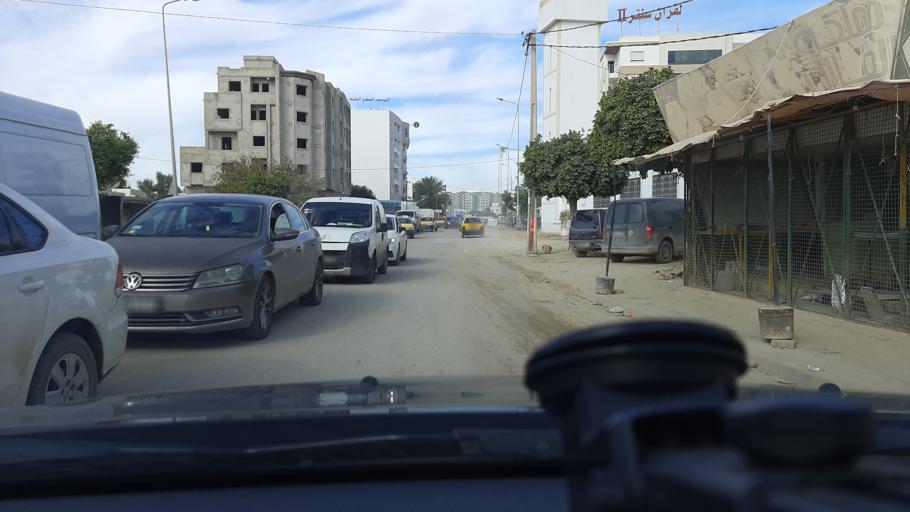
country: TN
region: Safaqis
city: Sfax
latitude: 34.7571
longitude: 10.7345
